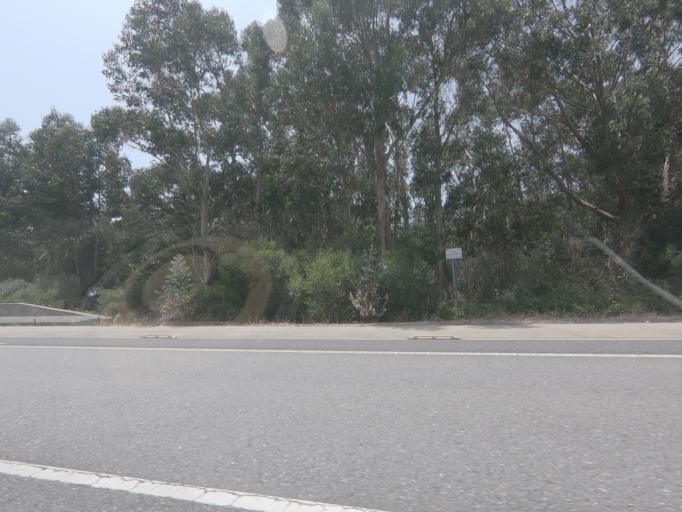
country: ES
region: Galicia
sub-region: Provincia de Pontevedra
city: A Guarda
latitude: 41.9181
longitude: -8.8798
